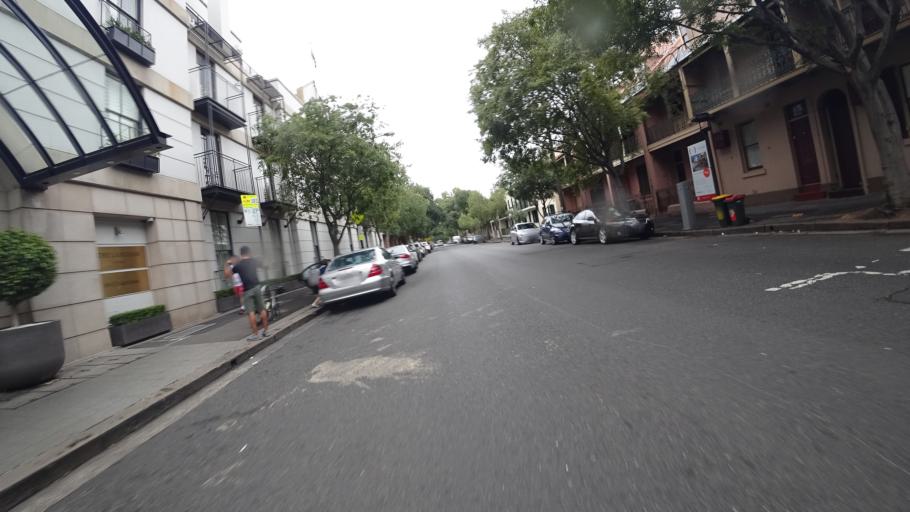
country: AU
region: New South Wales
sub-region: City of Sydney
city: Sydney
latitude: -33.8605
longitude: 151.2036
